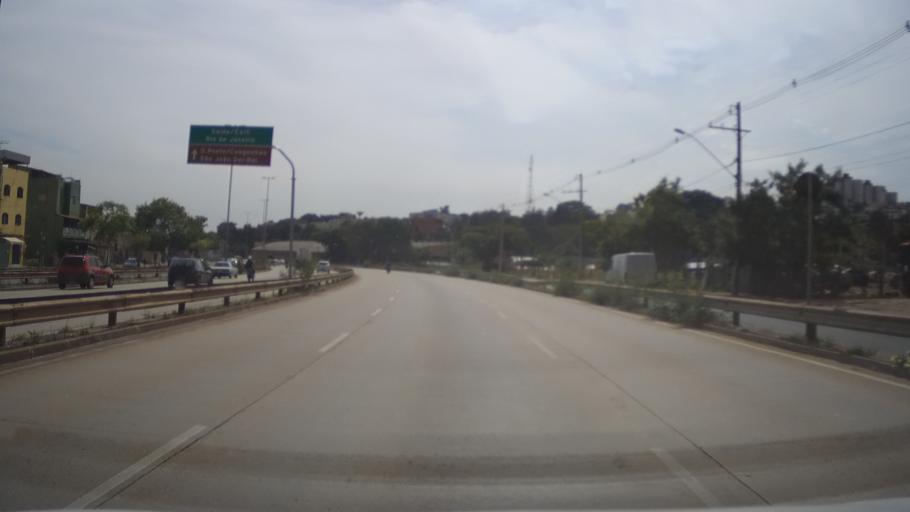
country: BR
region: Minas Gerais
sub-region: Contagem
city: Contagem
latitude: -19.9360
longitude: -43.9975
